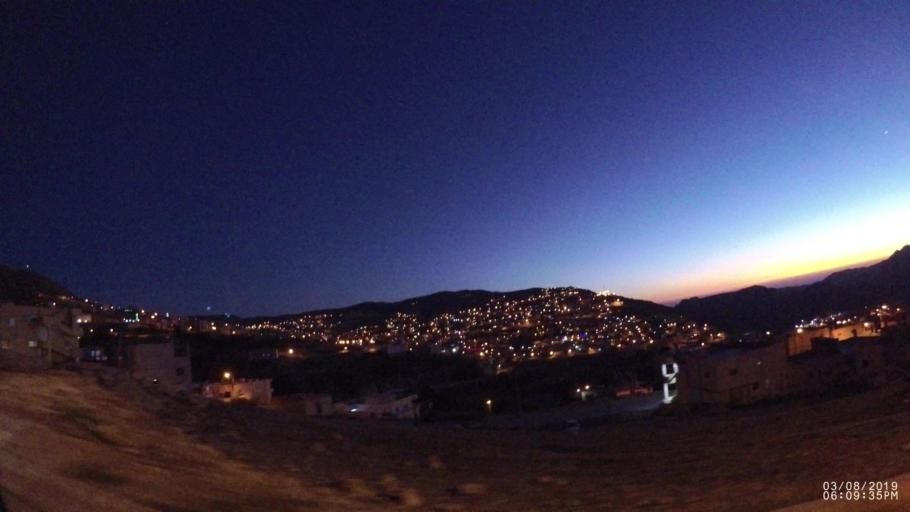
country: JO
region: Ma'an
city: Petra
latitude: 30.3291
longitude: 35.4818
